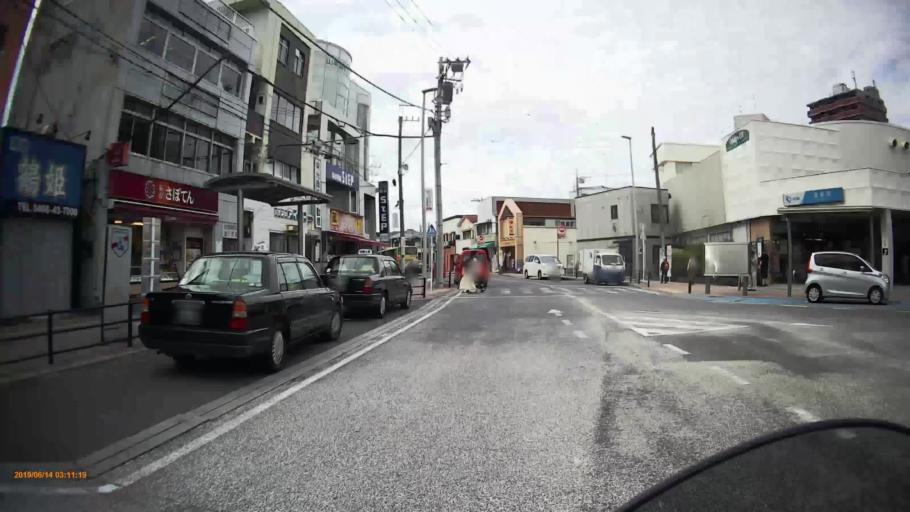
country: JP
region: Kanagawa
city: Fujisawa
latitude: 35.4125
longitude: 139.4648
